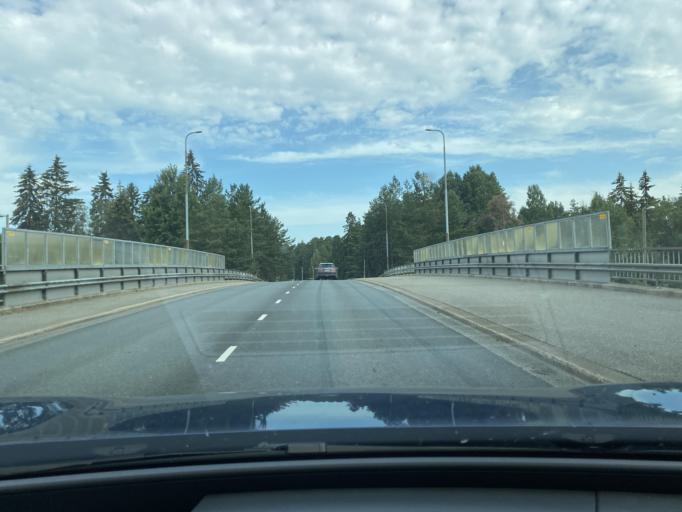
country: FI
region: Pirkanmaa
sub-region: Lounais-Pirkanmaa
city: Vammala
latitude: 61.3504
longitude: 22.8982
